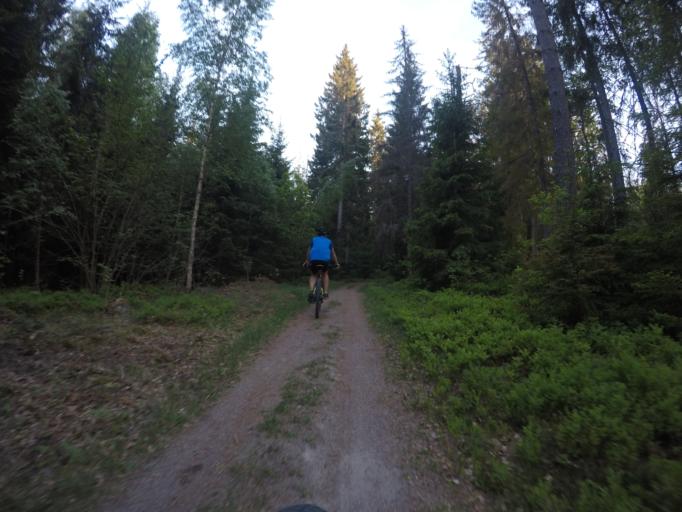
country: SE
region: Soedermanland
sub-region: Eskilstuna Kommun
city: Skogstorp
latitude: 59.3389
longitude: 16.5045
